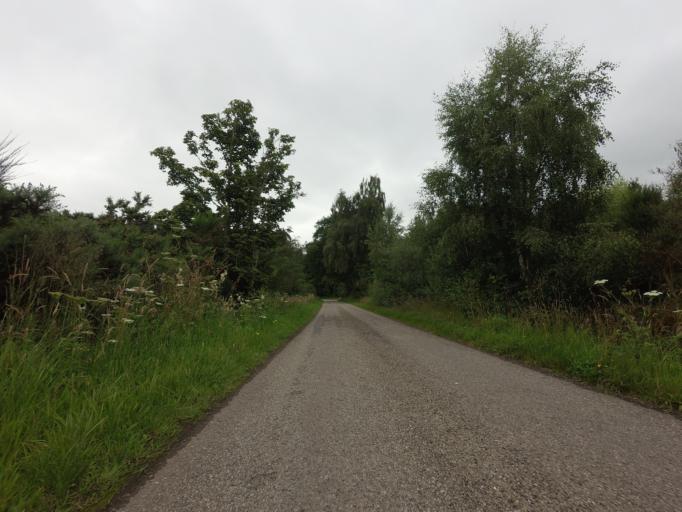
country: GB
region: Scotland
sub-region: Highland
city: Evanton
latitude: 57.8904
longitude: -4.3818
